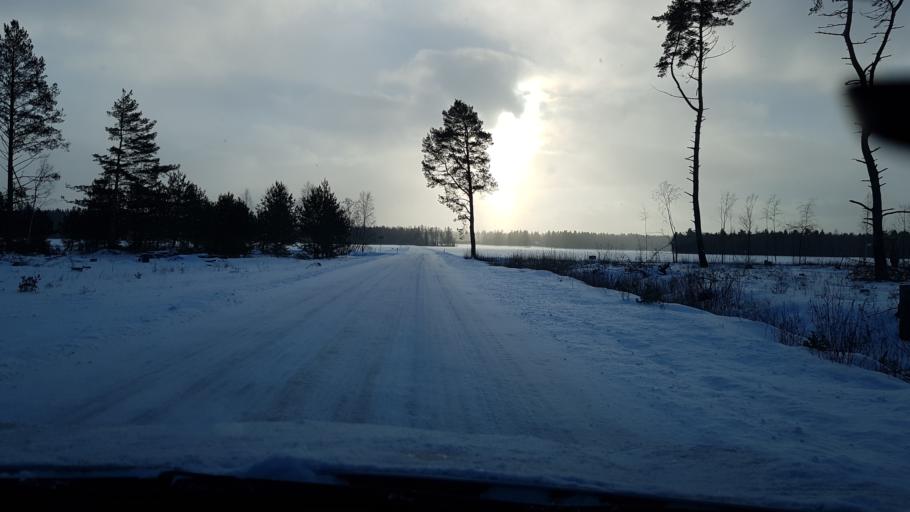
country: EE
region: Harju
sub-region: Nissi vald
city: Turba
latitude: 59.2062
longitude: 24.1406
